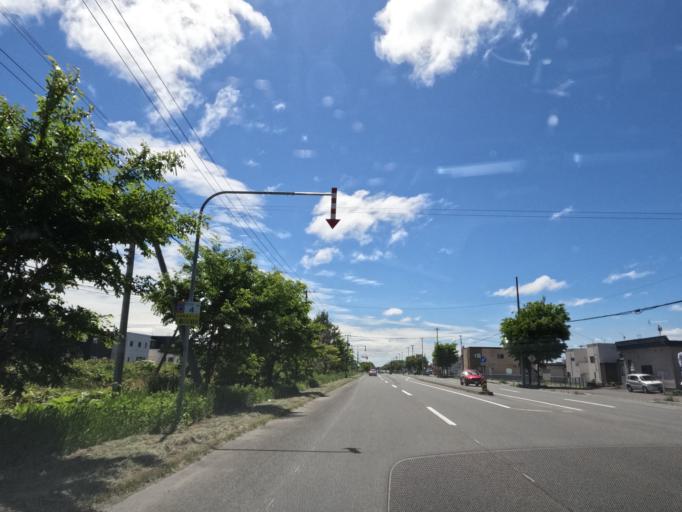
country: JP
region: Hokkaido
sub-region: Asahikawa-shi
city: Asahikawa
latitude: 43.7410
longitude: 142.3598
